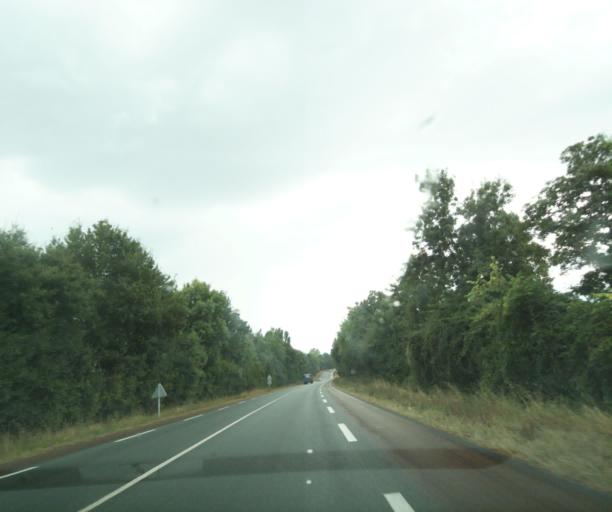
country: FR
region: Poitou-Charentes
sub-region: Departement de la Charente-Maritime
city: Cabariot
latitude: 45.9432
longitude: -0.8645
